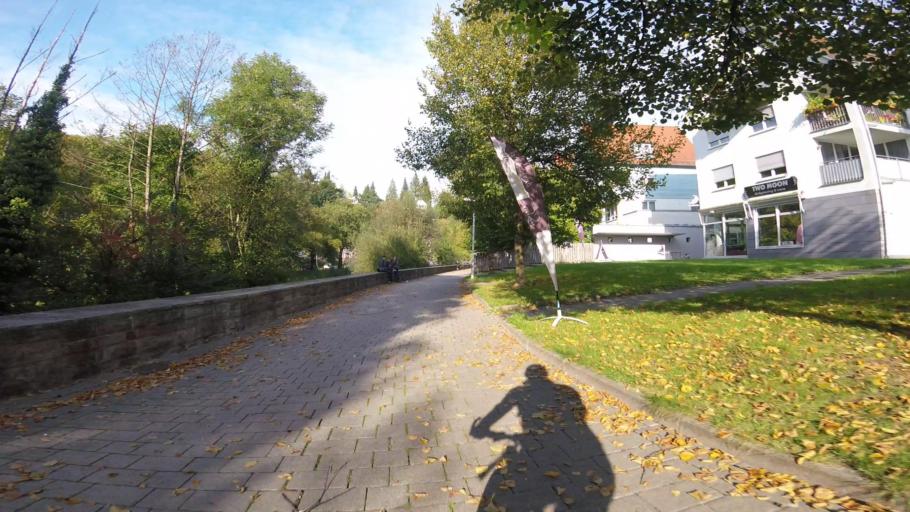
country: DE
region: Baden-Wuerttemberg
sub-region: Regierungsbezirk Stuttgart
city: Backnang
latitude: 48.9486
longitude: 9.4286
